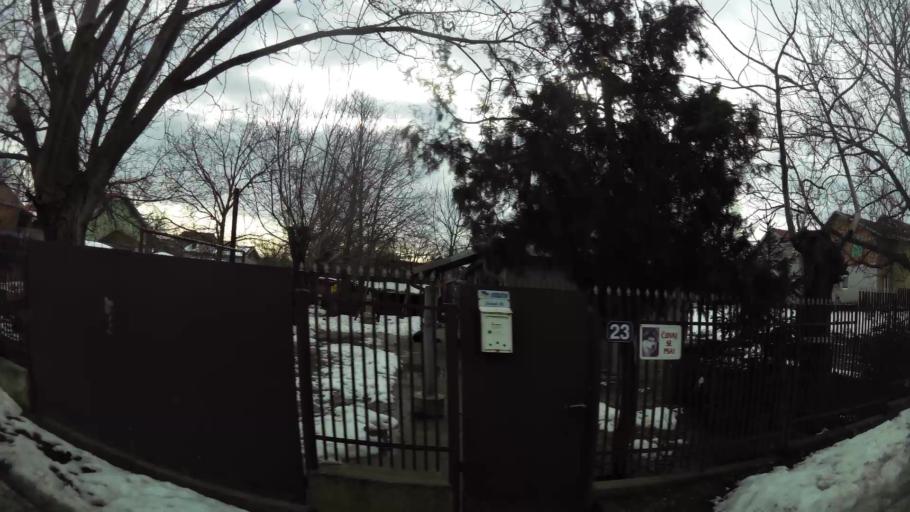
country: RS
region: Central Serbia
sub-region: Belgrade
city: Surcin
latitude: 44.8038
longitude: 20.3308
